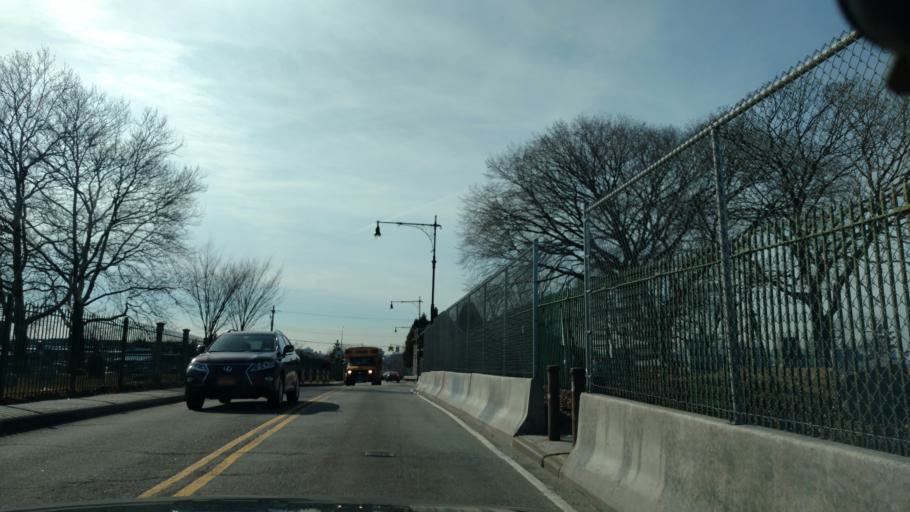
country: US
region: New York
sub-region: Kings County
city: East New York
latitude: 40.7170
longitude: -73.8963
